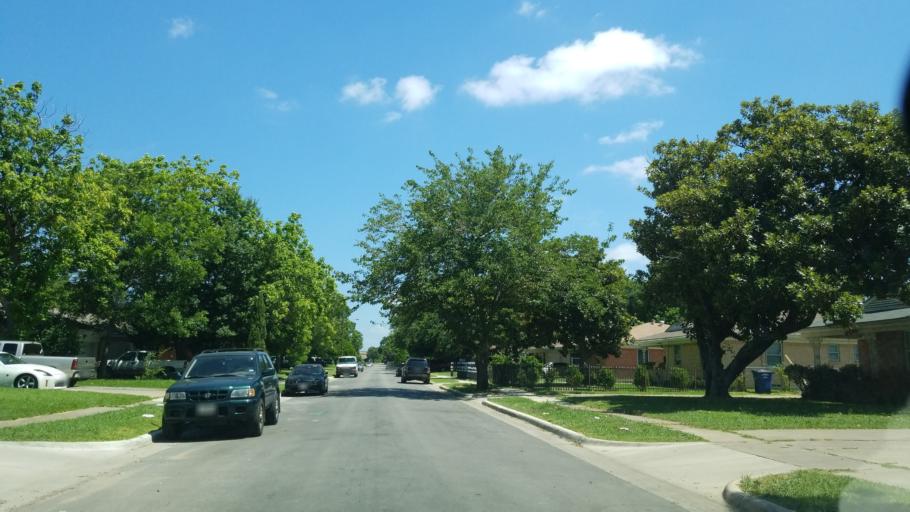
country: US
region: Texas
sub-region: Dallas County
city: Balch Springs
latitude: 32.7425
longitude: -96.6941
